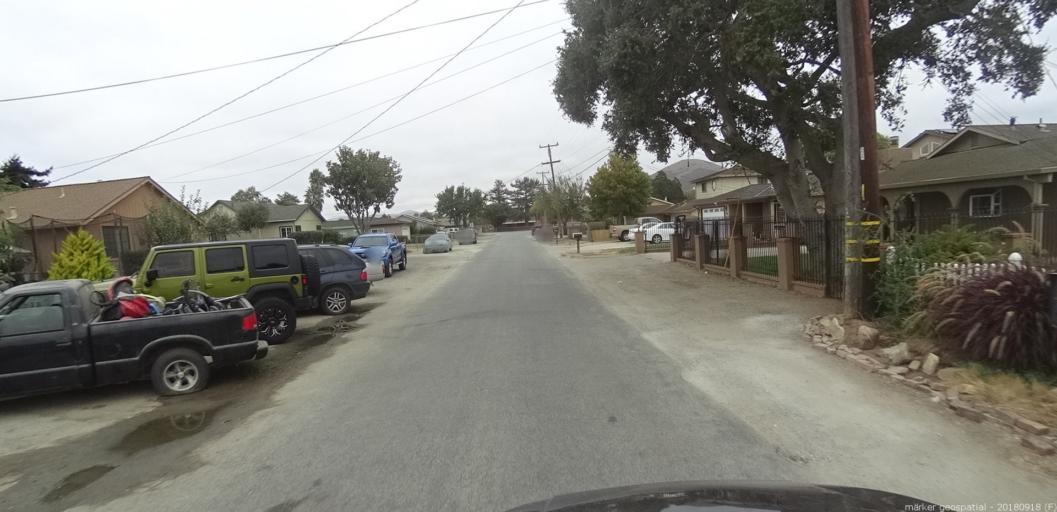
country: US
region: California
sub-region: Monterey County
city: Prunedale
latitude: 36.7574
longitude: -121.6144
